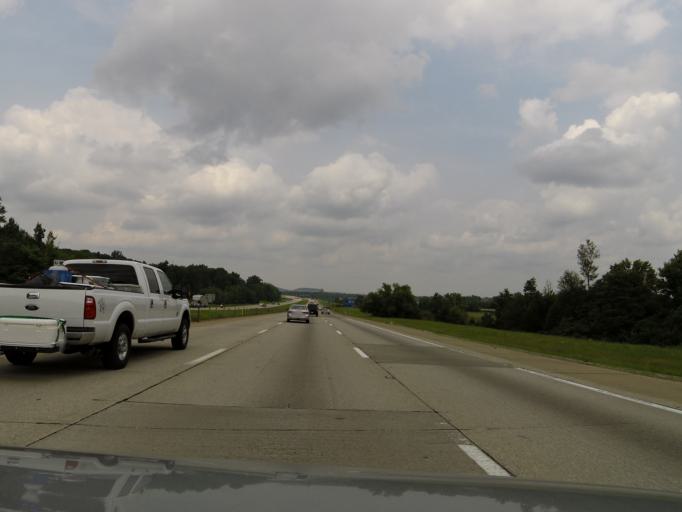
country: US
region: Kentucky
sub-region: Bullitt County
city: Shepherdsville
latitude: 37.9632
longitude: -85.6942
